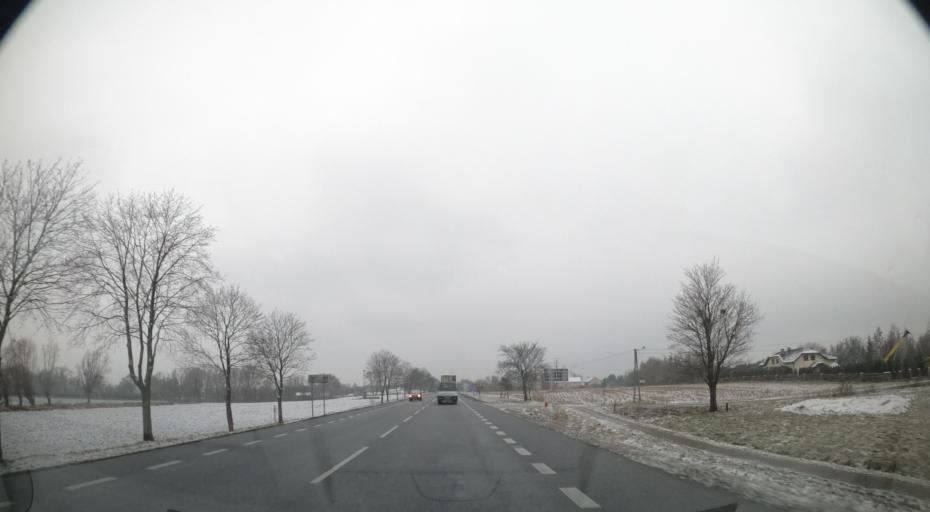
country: PL
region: Masovian Voivodeship
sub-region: Powiat sochaczewski
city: Paprotnia
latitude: 52.2084
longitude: 20.4684
